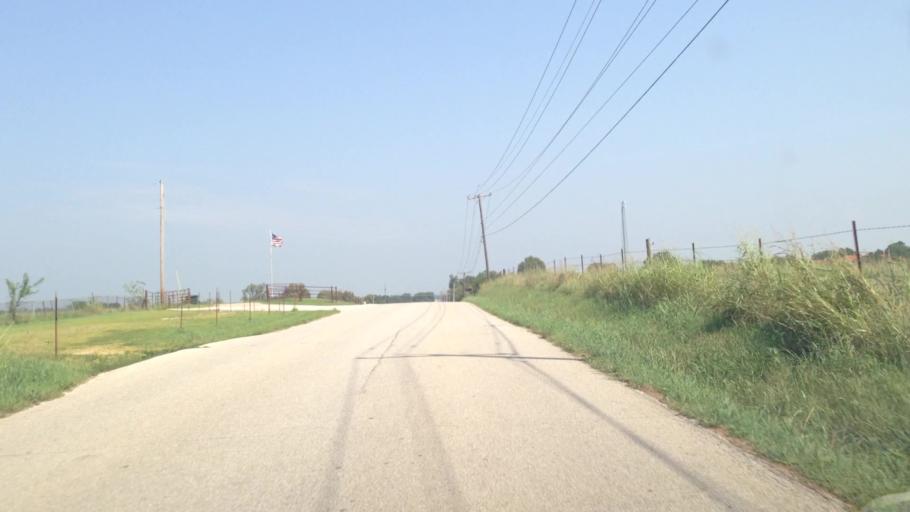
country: US
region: Oklahoma
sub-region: Craig County
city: Vinita
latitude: 36.6516
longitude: -95.1256
